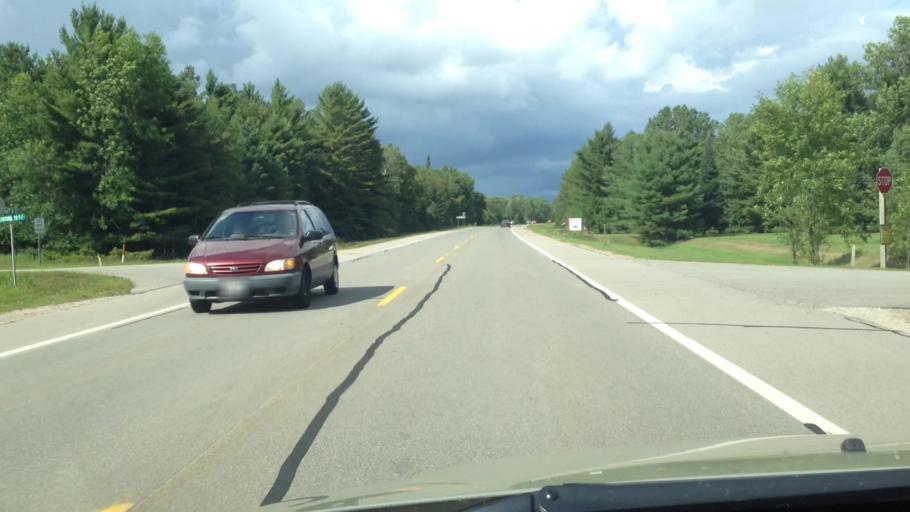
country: US
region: Michigan
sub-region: Menominee County
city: Menominee
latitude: 45.3205
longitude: -87.4309
